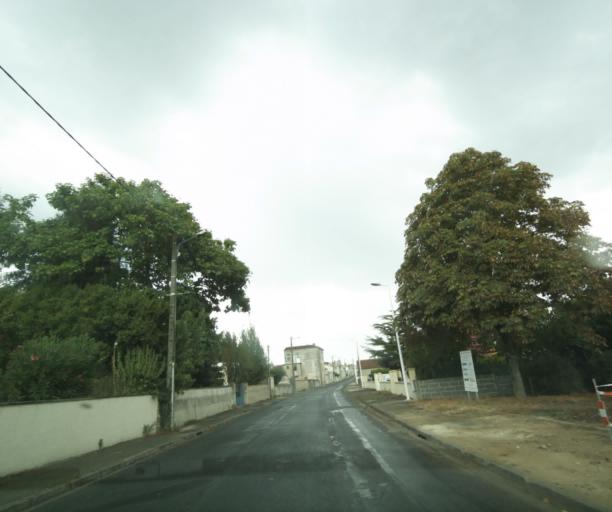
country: FR
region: Poitou-Charentes
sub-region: Departement de la Charente-Maritime
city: Tonnay-Charente
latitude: 45.9462
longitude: -0.8818
